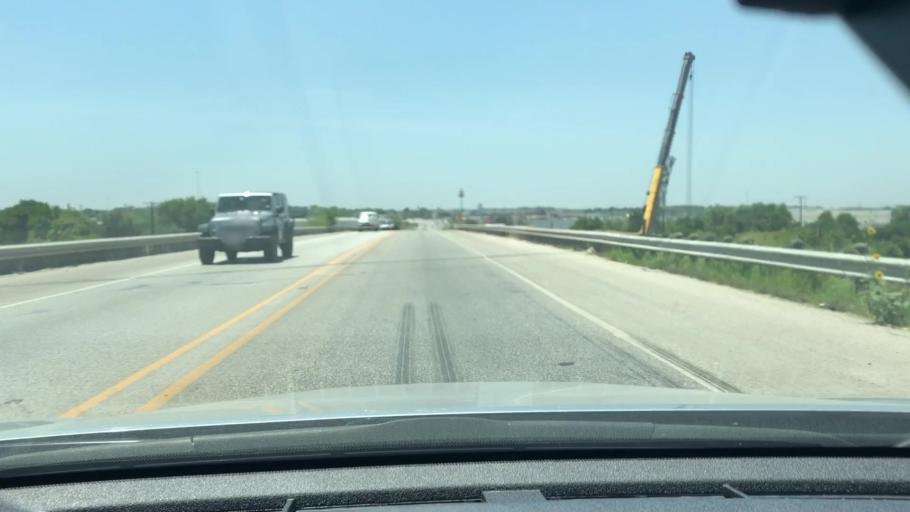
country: US
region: Texas
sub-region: Comal County
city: New Braunfels
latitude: 29.6834
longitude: -98.1536
